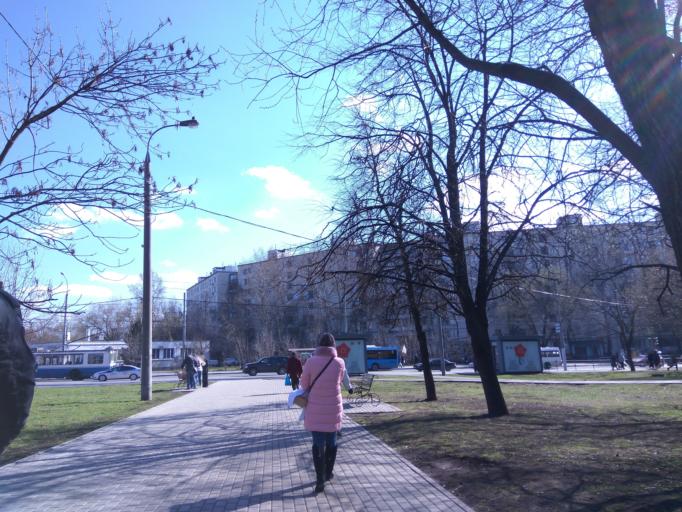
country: RU
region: Moscow
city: Ivanovskoye
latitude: 55.7682
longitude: 37.8383
